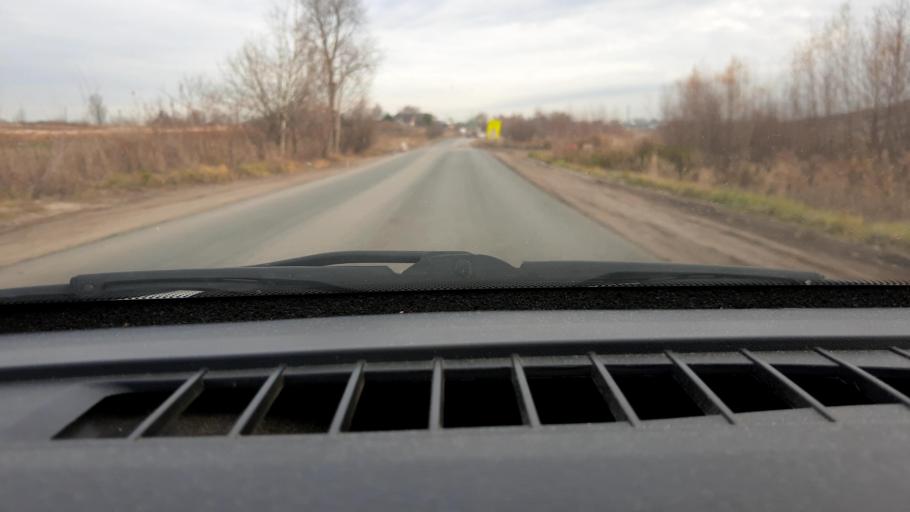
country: RU
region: Nizjnij Novgorod
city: Neklyudovo
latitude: 56.4210
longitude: 43.9575
